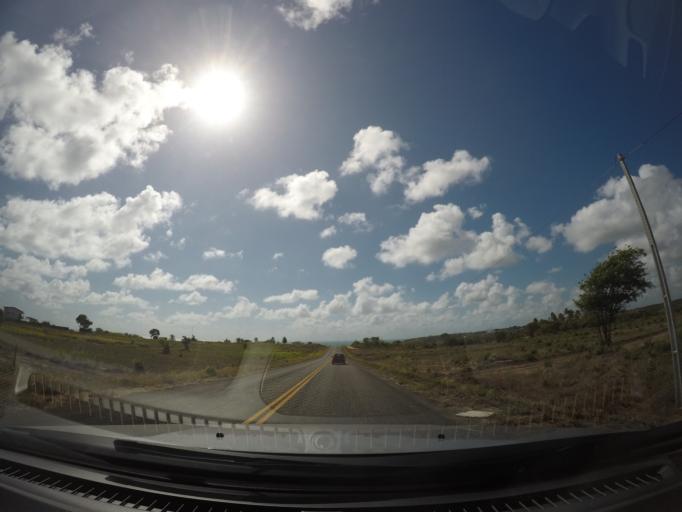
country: BR
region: Paraiba
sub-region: Pitimbu
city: Pitimbu
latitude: -7.3931
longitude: -34.8137
